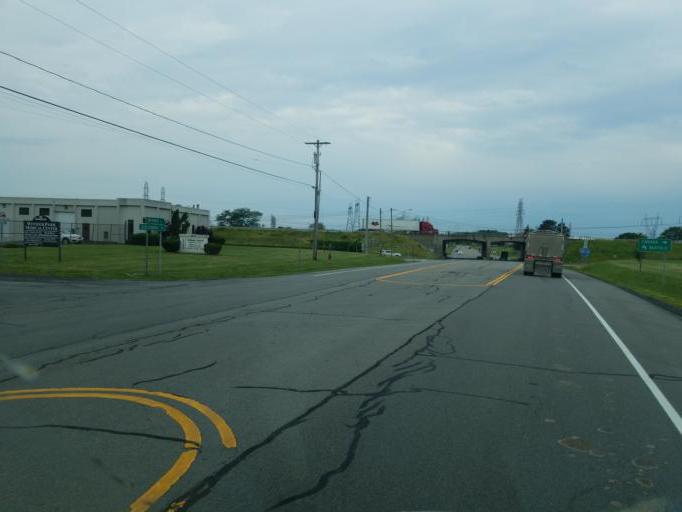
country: US
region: New York
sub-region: Niagara County
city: Lewiston
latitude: 43.1301
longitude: -79.0164
